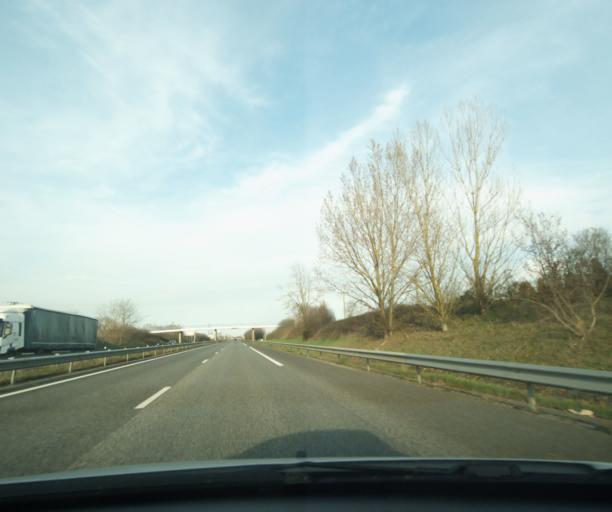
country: FR
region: Midi-Pyrenees
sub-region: Departement de la Haute-Garonne
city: Martres-Tolosane
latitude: 43.2028
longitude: 1.0091
